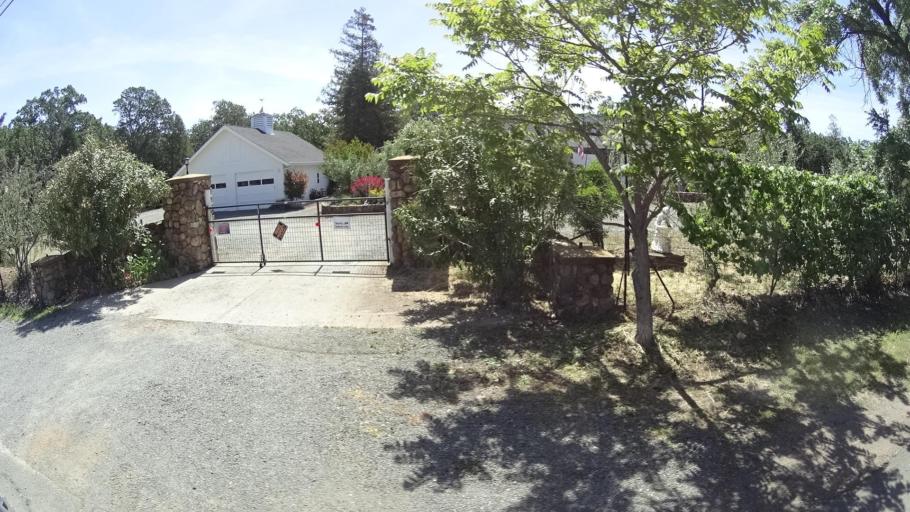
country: US
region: California
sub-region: Lake County
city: Middletown
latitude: 38.7488
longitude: -122.6236
